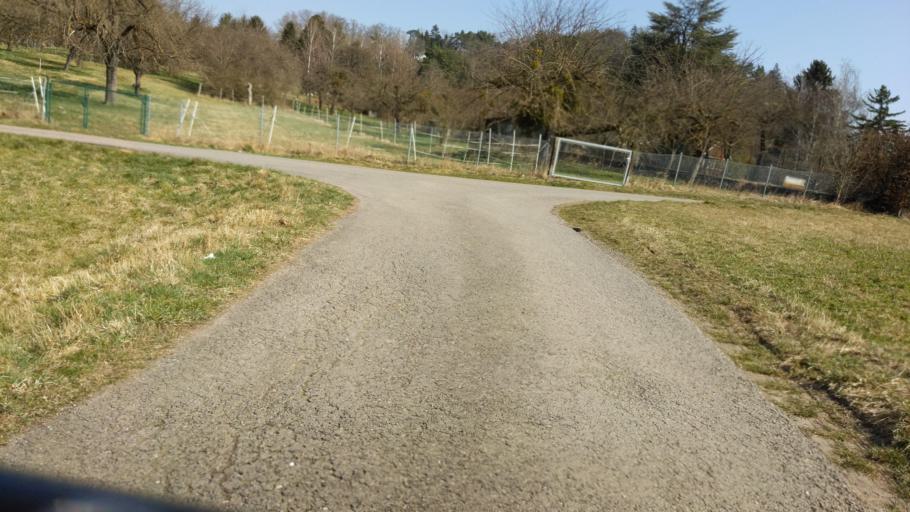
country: DE
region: Baden-Wuerttemberg
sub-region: Regierungsbezirk Stuttgart
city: Leonberg
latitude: 48.7785
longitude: 9.0341
